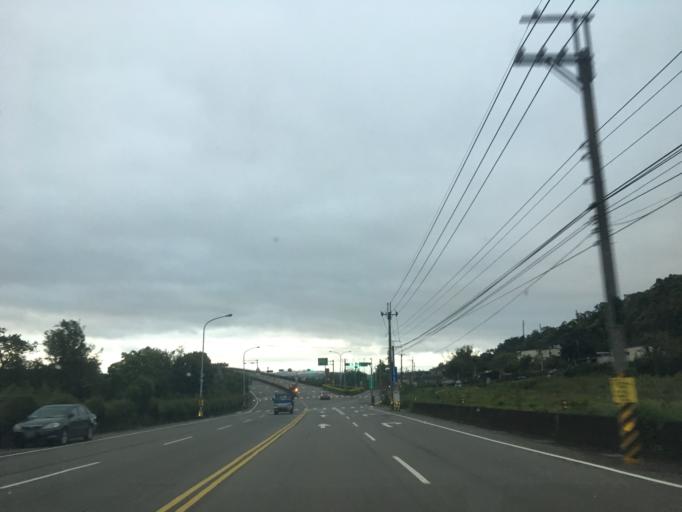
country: TW
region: Taiwan
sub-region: Miaoli
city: Miaoli
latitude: 24.4567
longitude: 120.7812
